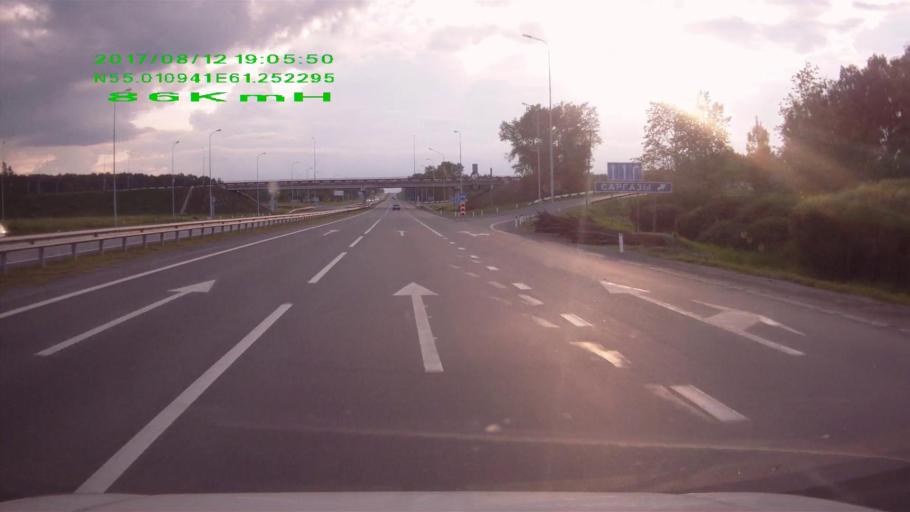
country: RU
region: Chelyabinsk
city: Sargazy
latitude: 55.0098
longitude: 61.2352
